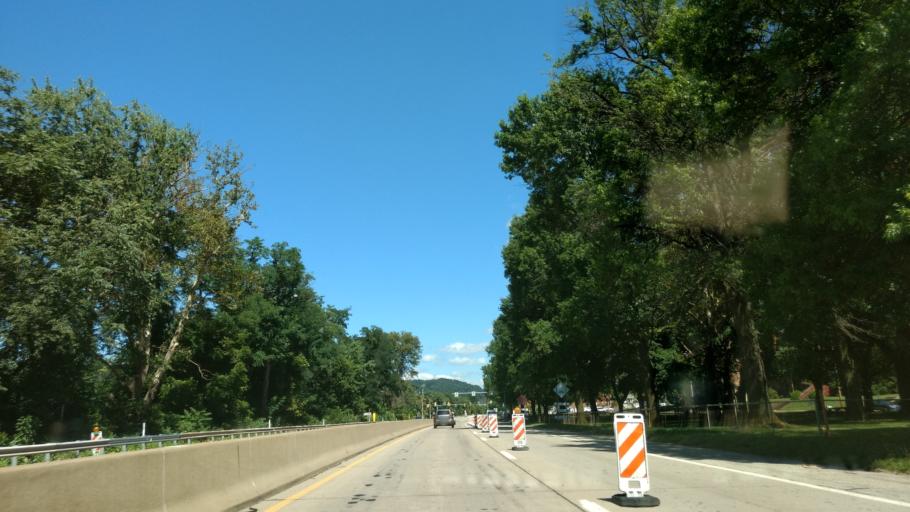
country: US
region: Pennsylvania
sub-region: Beaver County
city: Ambridge
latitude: 40.5866
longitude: -80.2307
